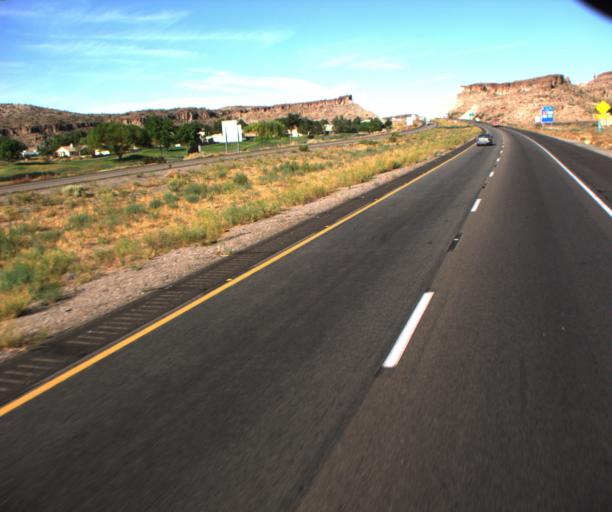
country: US
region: Arizona
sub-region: Mohave County
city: Kingman
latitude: 35.2148
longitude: -114.0475
